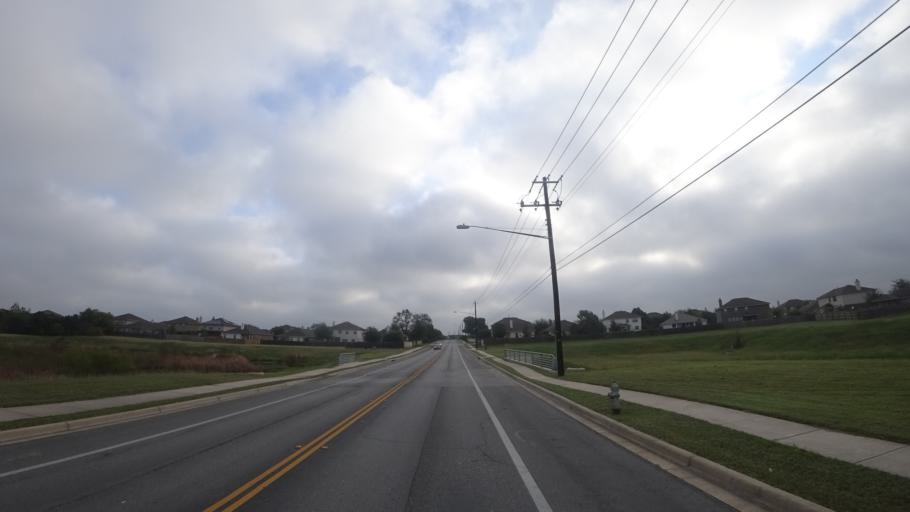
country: US
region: Texas
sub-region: Travis County
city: Pflugerville
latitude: 30.3596
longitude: -97.6462
